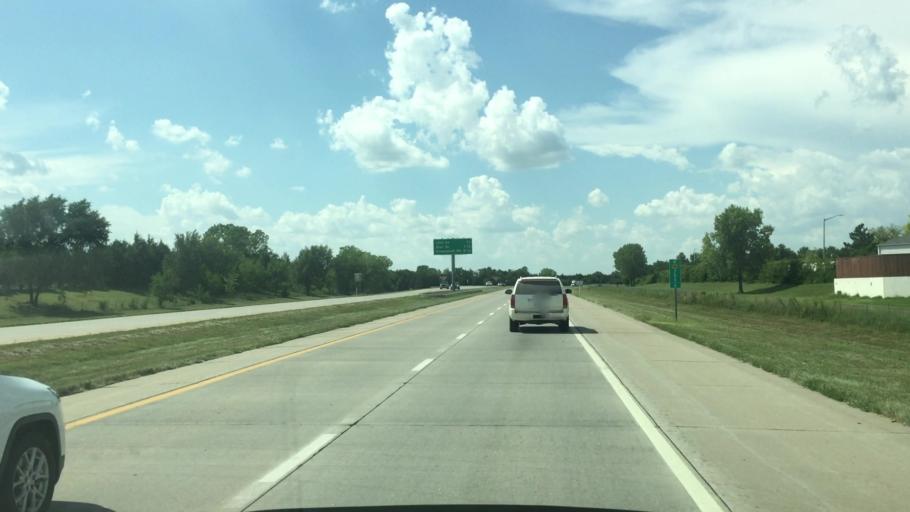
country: US
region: Kansas
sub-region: Butler County
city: Andover
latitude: 37.6984
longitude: -97.1933
